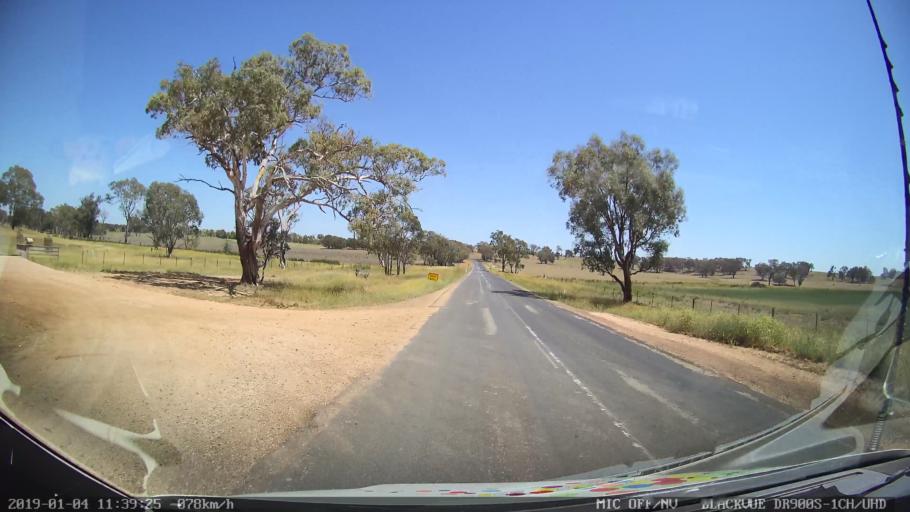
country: AU
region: New South Wales
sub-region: Cabonne
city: Molong
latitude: -33.0135
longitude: 148.7958
